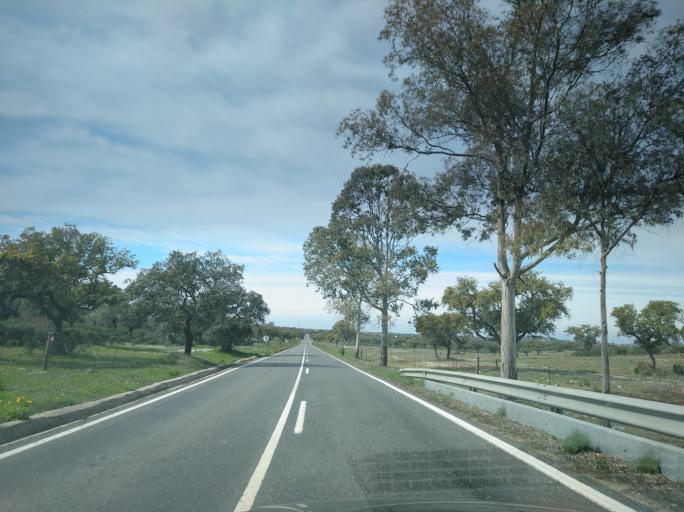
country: PT
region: Beja
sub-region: Mertola
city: Mertola
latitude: 37.7367
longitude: -7.7740
